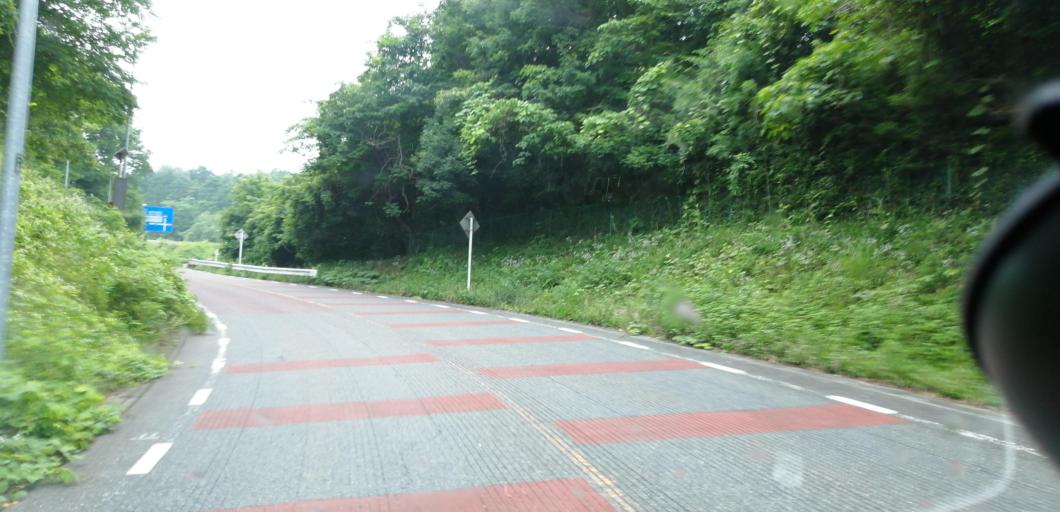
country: JP
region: Saitama
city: Yorii
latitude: 36.1134
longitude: 139.1711
